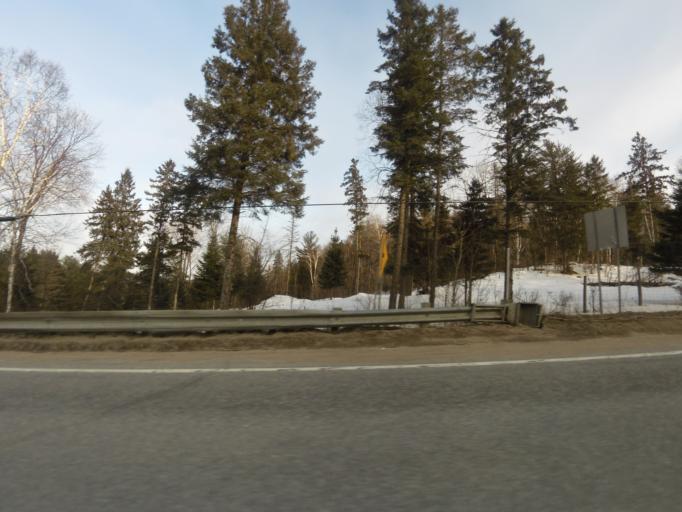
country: CA
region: Quebec
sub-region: Outaouais
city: Wakefield
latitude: 45.9350
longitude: -76.0057
